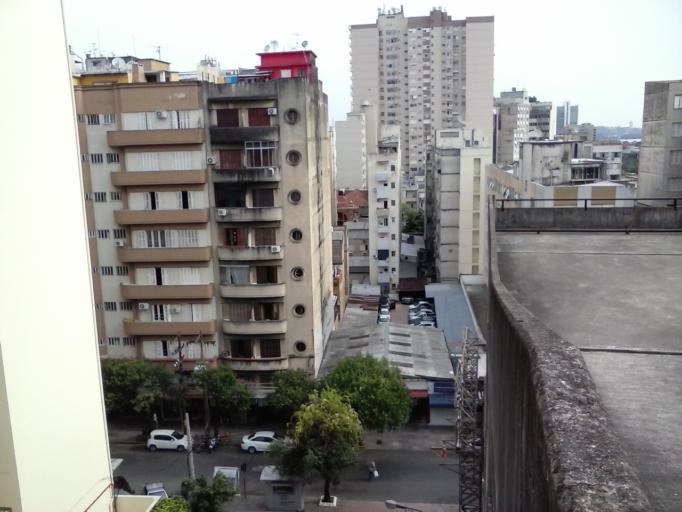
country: BR
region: Rio Grande do Sul
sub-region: Porto Alegre
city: Porto Alegre
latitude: -30.0346
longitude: -51.2285
